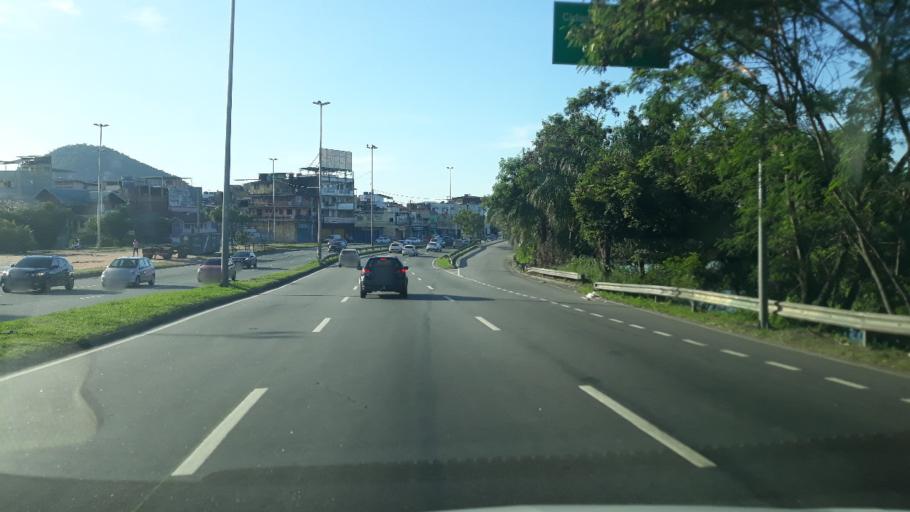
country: BR
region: Rio de Janeiro
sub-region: Sao Joao De Meriti
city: Sao Joao de Meriti
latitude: -22.9556
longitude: -43.3570
